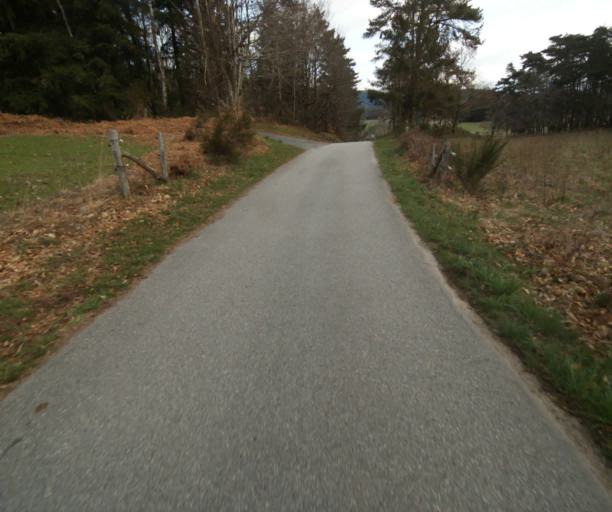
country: FR
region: Limousin
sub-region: Departement de la Correze
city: Correze
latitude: 45.3881
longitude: 1.8802
